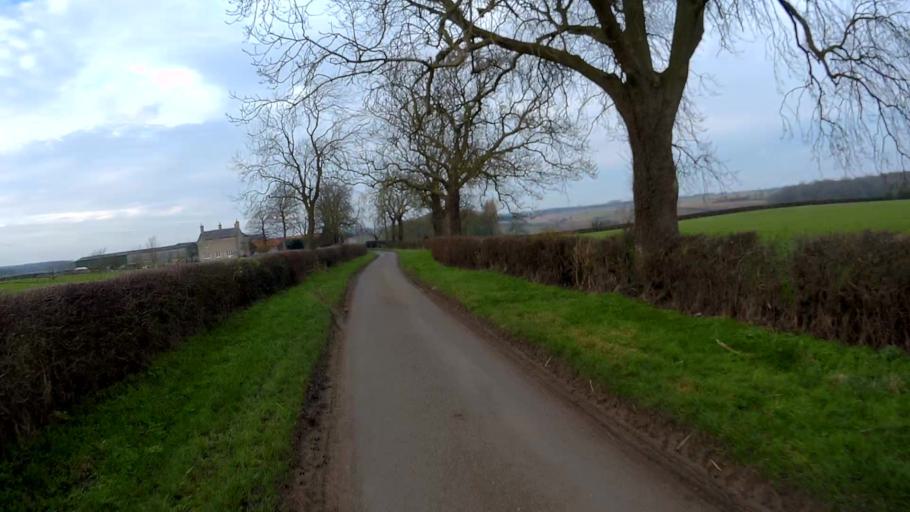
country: GB
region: England
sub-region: Lincolnshire
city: Bourne
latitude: 52.8228
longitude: -0.4580
